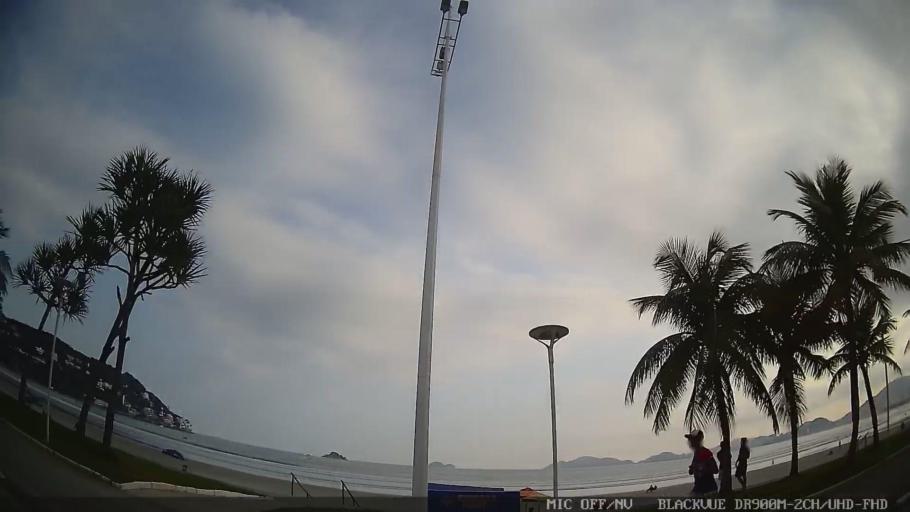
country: BR
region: Sao Paulo
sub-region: Guaruja
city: Guaruja
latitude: -23.9881
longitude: -46.2050
